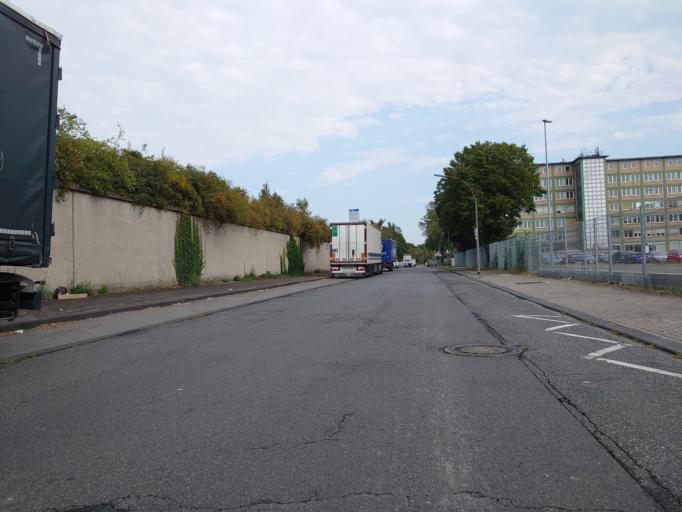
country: DE
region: North Rhine-Westphalia
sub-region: Regierungsbezirk Koln
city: Bilderstoeckchen
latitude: 50.9995
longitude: 6.9476
